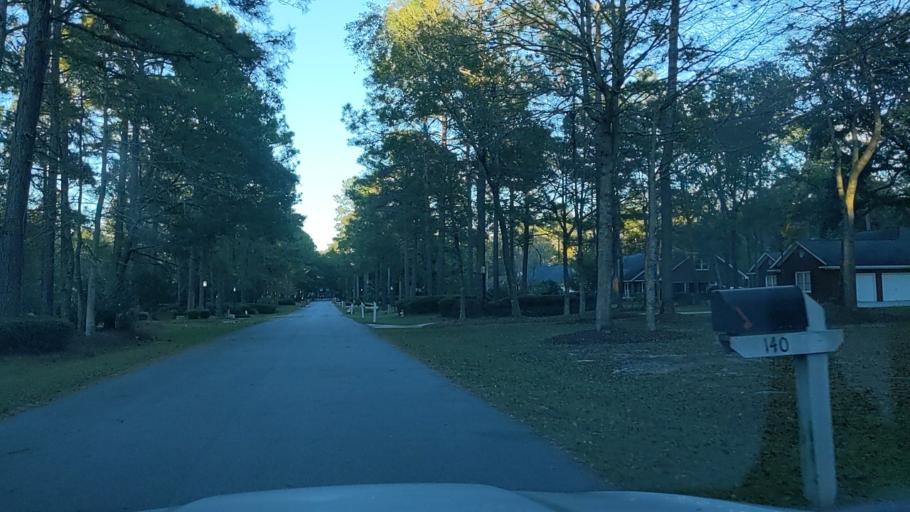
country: US
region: Georgia
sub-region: Effingham County
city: Rincon
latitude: 32.2651
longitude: -81.2102
